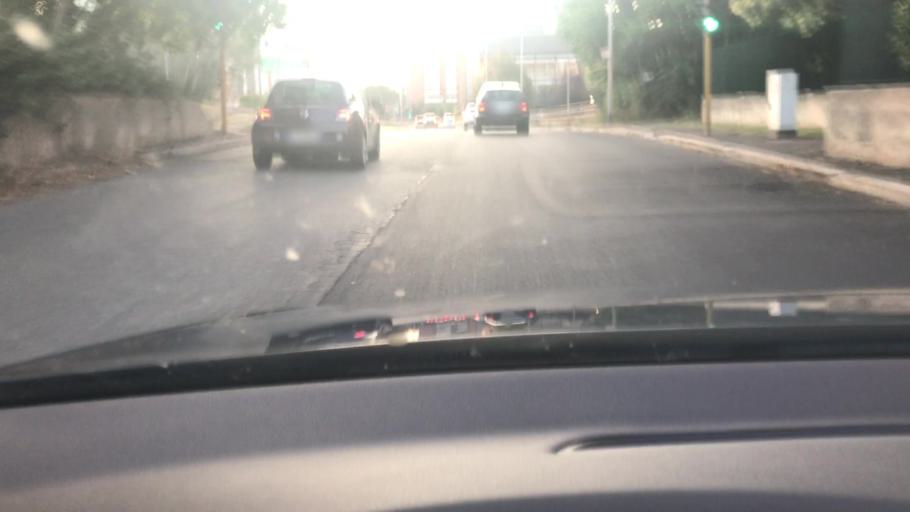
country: IT
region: Latium
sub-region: Citta metropolitana di Roma Capitale
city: Rome
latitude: 41.9295
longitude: 12.5626
